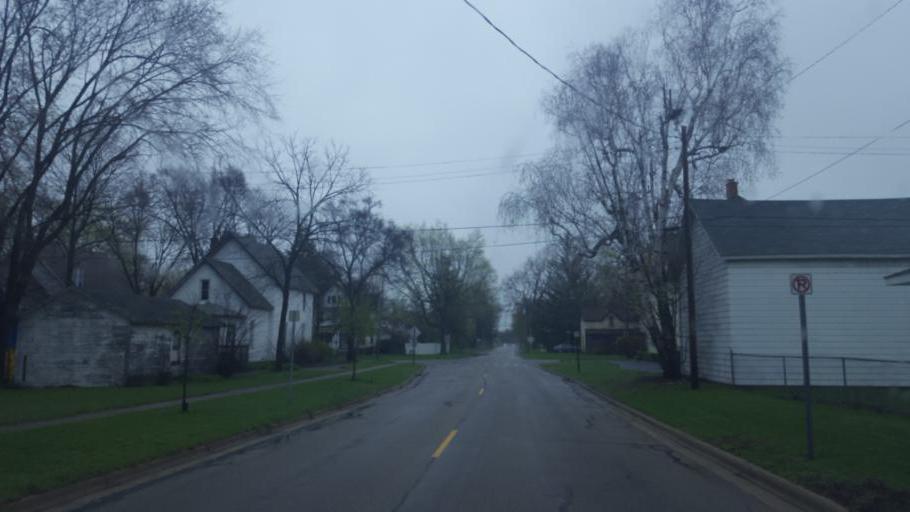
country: US
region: Michigan
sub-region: Isabella County
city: Mount Pleasant
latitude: 43.6054
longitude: -84.7730
